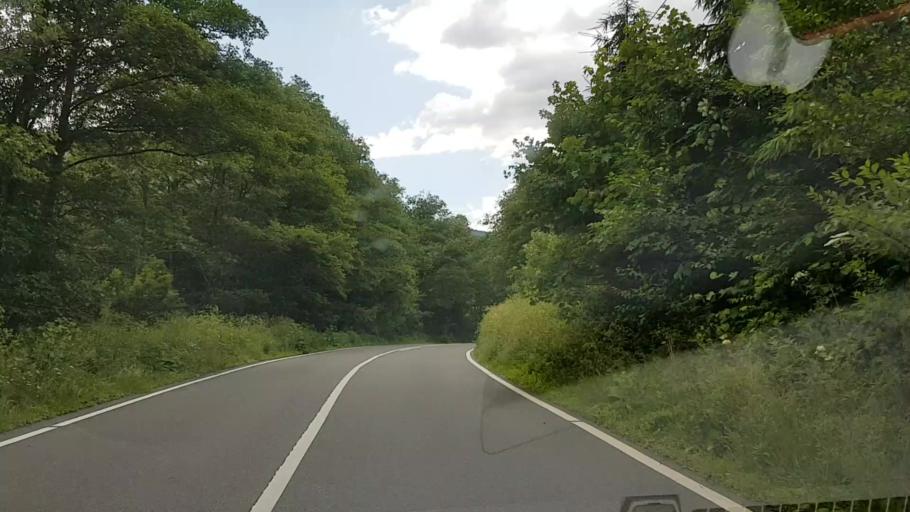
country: RO
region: Suceava
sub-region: Comuna Crucea
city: Crucea
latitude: 47.3281
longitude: 25.6206
